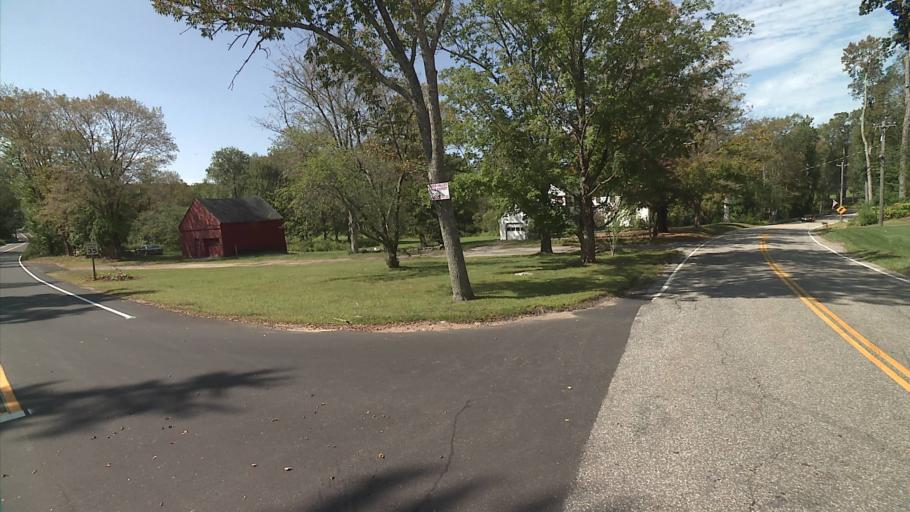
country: US
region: Connecticut
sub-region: Tolland County
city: Coventry Lake
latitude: 41.7324
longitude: -72.3726
